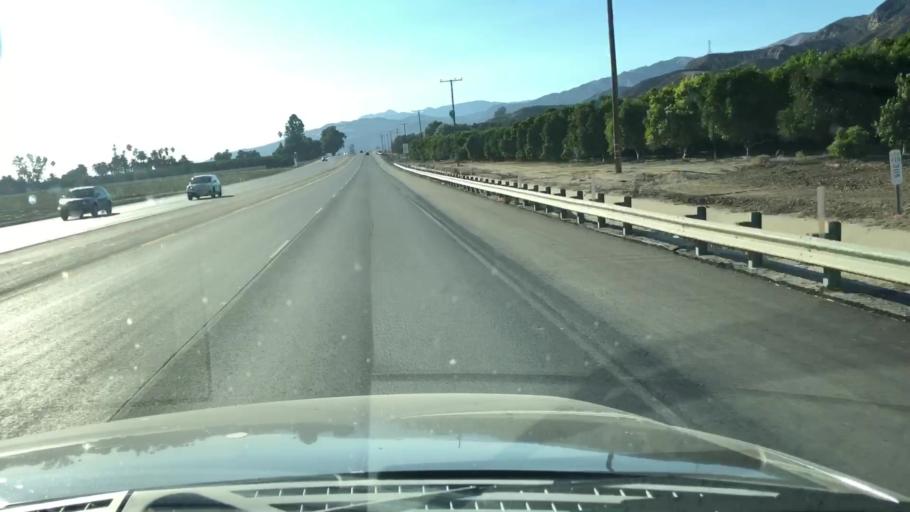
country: US
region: California
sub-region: Ventura County
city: Piru
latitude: 34.4060
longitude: -118.7475
